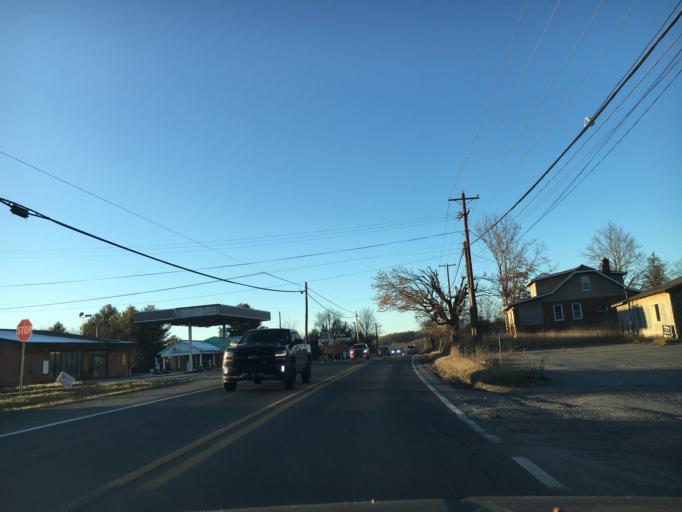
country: US
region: West Virginia
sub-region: Raleigh County
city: Daniels
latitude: 37.7434
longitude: -81.1230
